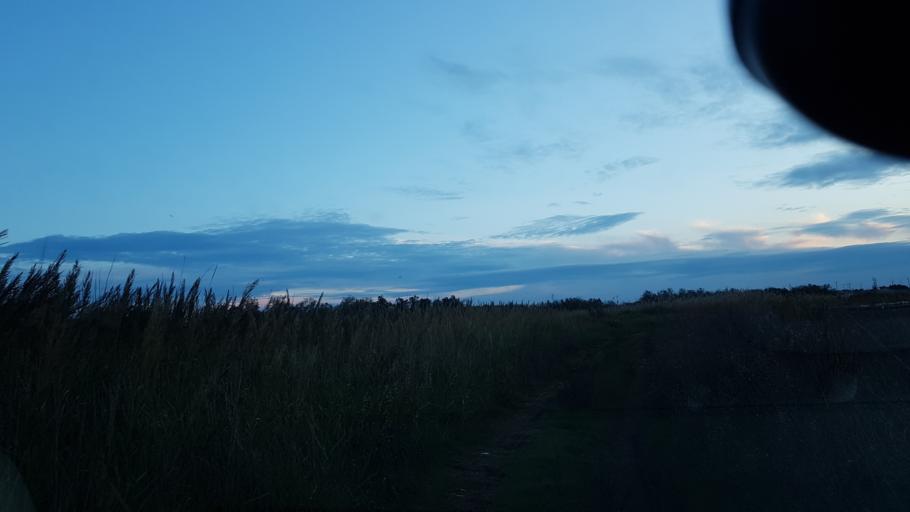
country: IT
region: Apulia
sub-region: Provincia di Brindisi
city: La Rosa
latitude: 40.6134
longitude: 18.0195
